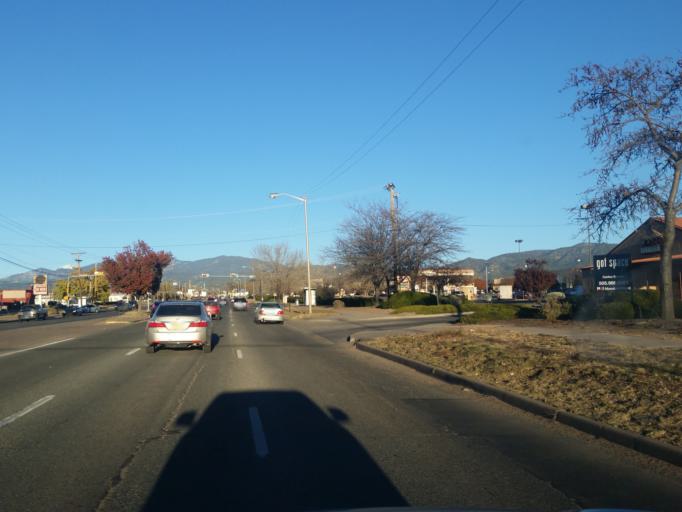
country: US
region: New Mexico
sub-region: Santa Fe County
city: Agua Fria
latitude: 35.6600
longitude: -105.9821
